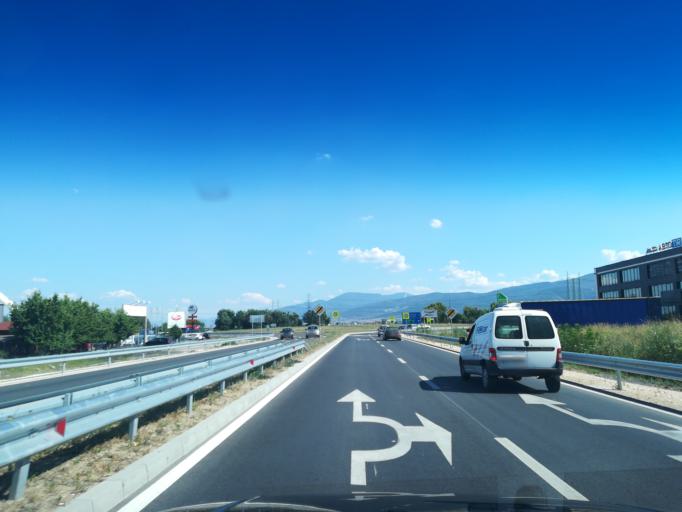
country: BG
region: Plovdiv
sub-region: Obshtina Plovdiv
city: Plovdiv
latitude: 42.1007
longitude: 24.7874
